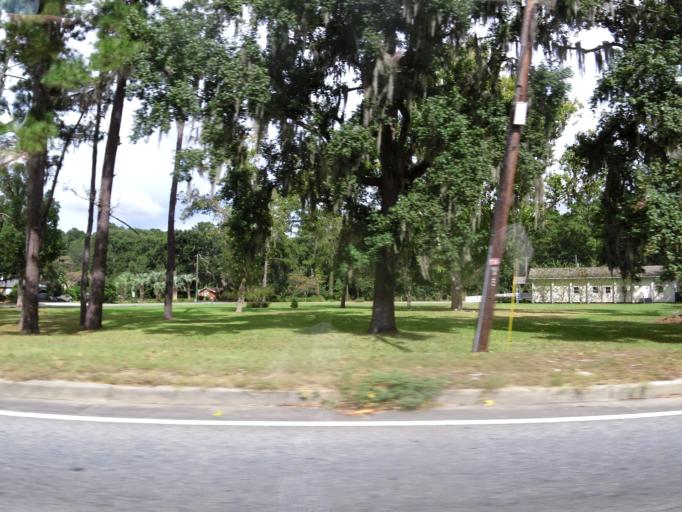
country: US
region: Georgia
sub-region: Glynn County
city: Dock Junction
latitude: 31.2097
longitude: -81.5116
